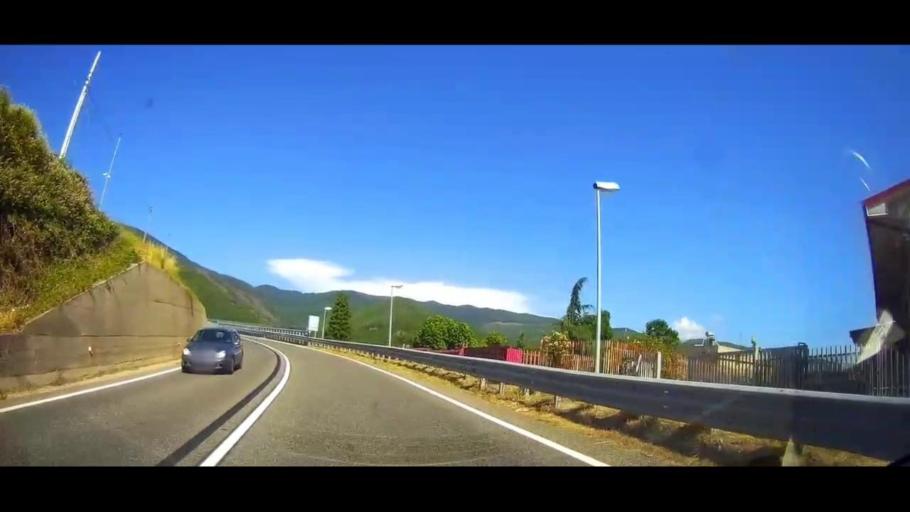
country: IT
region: Calabria
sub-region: Provincia di Cosenza
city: Spezzano Piccolo
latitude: 39.2932
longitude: 16.3451
